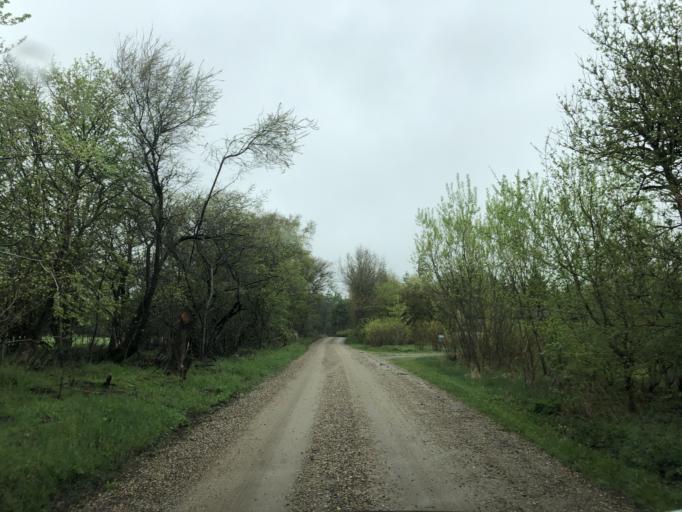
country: DK
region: Central Jutland
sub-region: Lemvig Kommune
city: Lemvig
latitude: 56.4473
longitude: 8.3870
